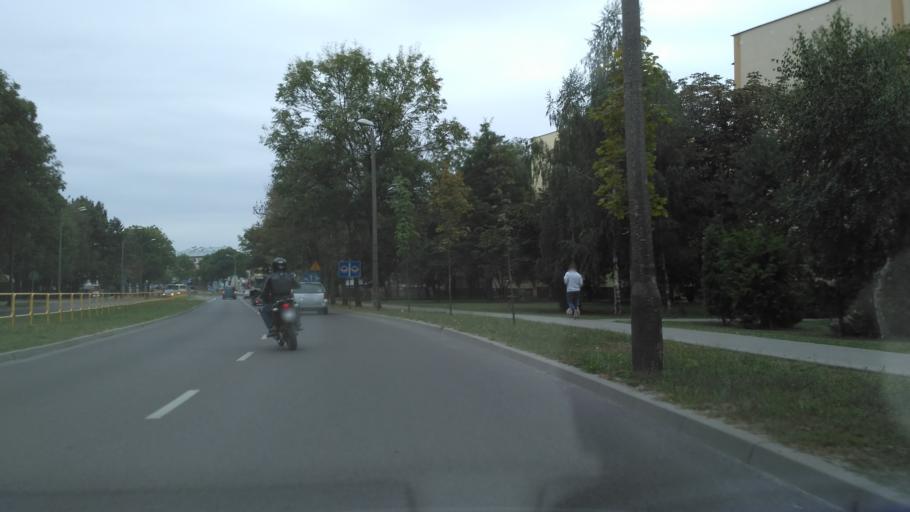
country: PL
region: Lublin Voivodeship
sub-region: Chelm
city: Chelm
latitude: 51.1336
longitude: 23.4640
